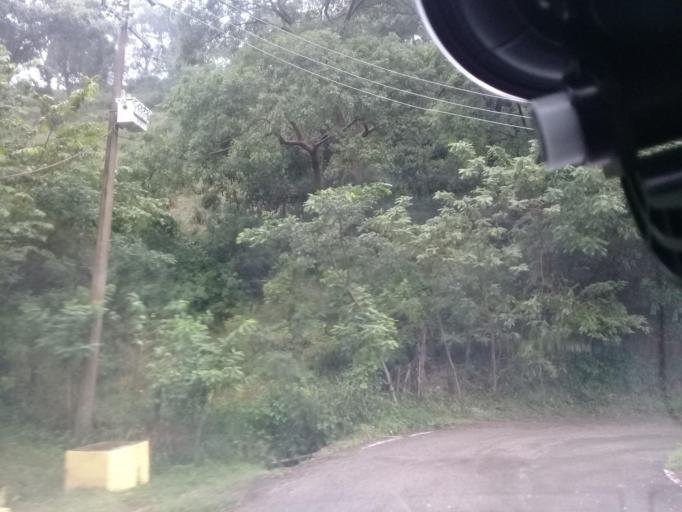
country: MX
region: Veracruz
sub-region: Chalma
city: San Pedro Coyutla
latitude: 21.2208
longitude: -98.4604
